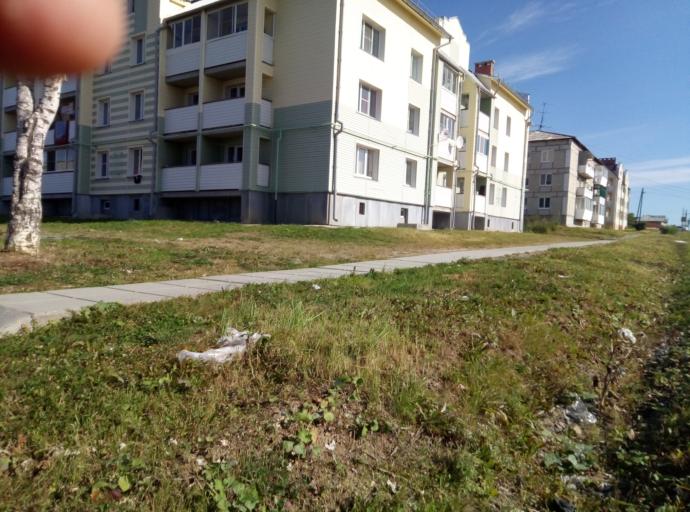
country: RU
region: Sverdlovsk
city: Karpinsk
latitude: 59.7801
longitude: 59.9920
